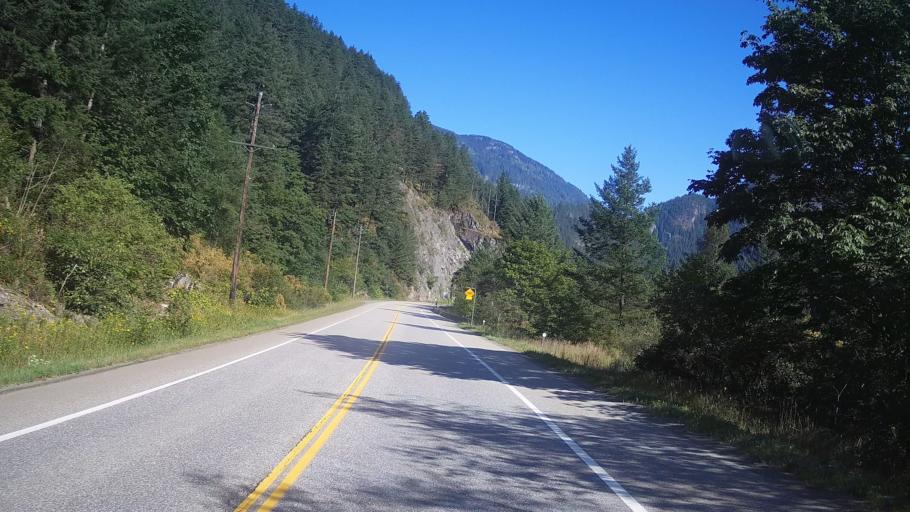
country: CA
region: British Columbia
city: Hope
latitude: 49.5880
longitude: -121.4062
